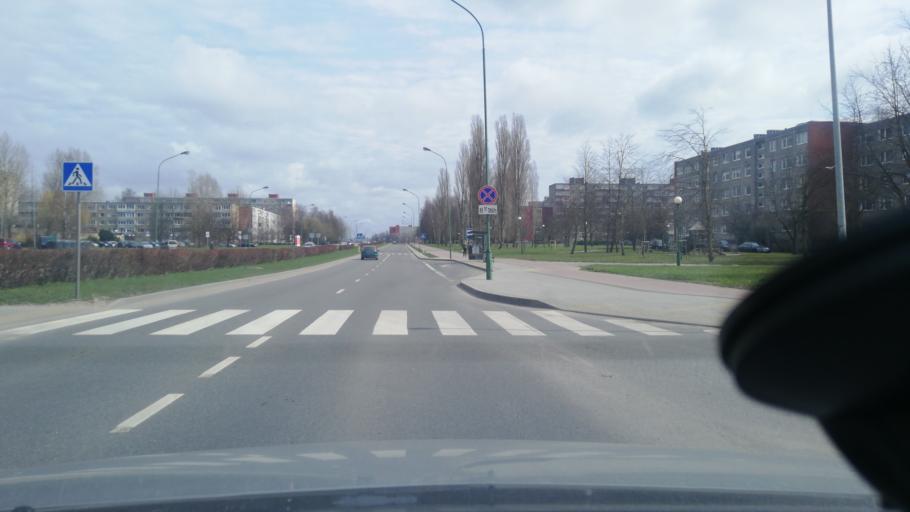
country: LT
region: Klaipedos apskritis
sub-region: Klaipeda
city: Klaipeda
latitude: 55.6731
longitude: 21.1714
